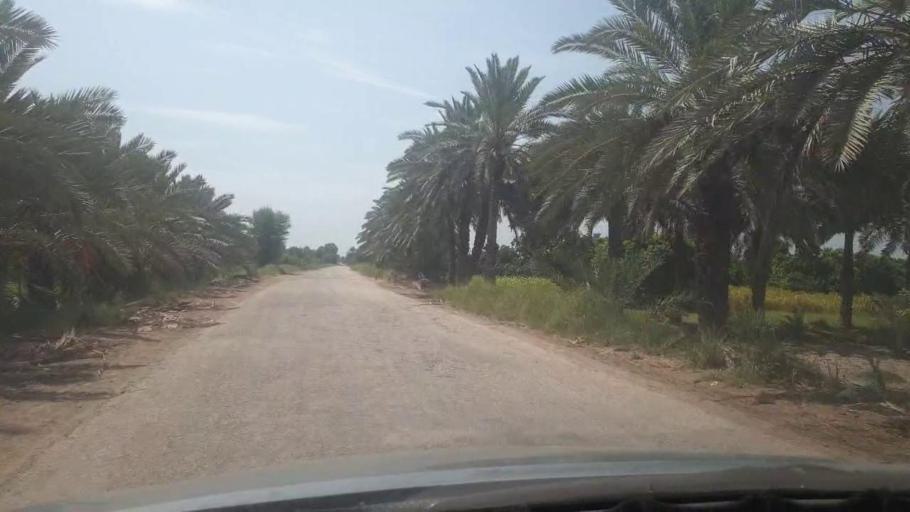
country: PK
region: Sindh
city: Bozdar
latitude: 27.2016
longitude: 68.5832
